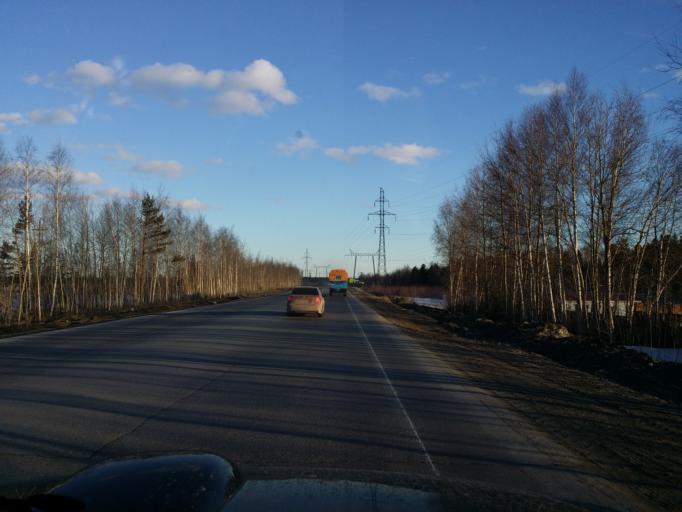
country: RU
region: Khanty-Mansiyskiy Avtonomnyy Okrug
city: Nizhnevartovsk
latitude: 61.0395
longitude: 76.3546
